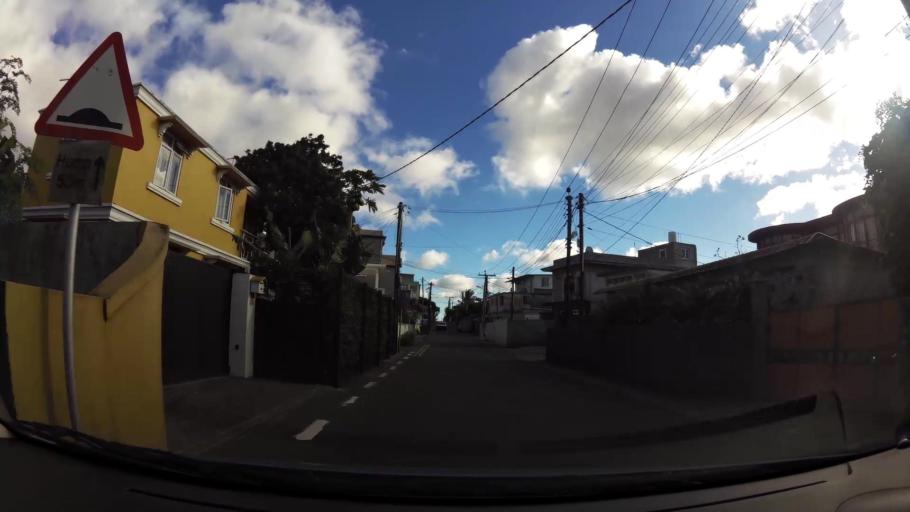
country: MU
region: Plaines Wilhems
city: Curepipe
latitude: -20.2942
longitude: 57.5175
